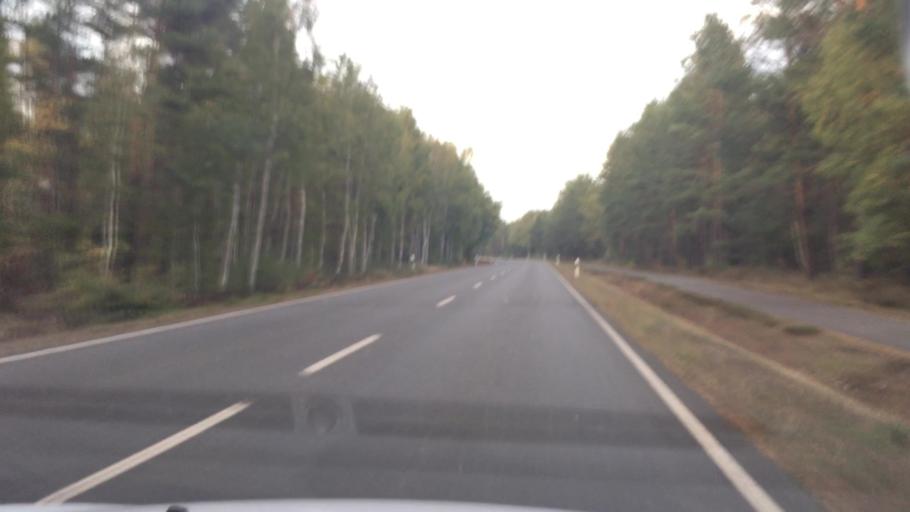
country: DE
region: Brandenburg
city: Schipkau
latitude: 51.4955
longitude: 13.8942
